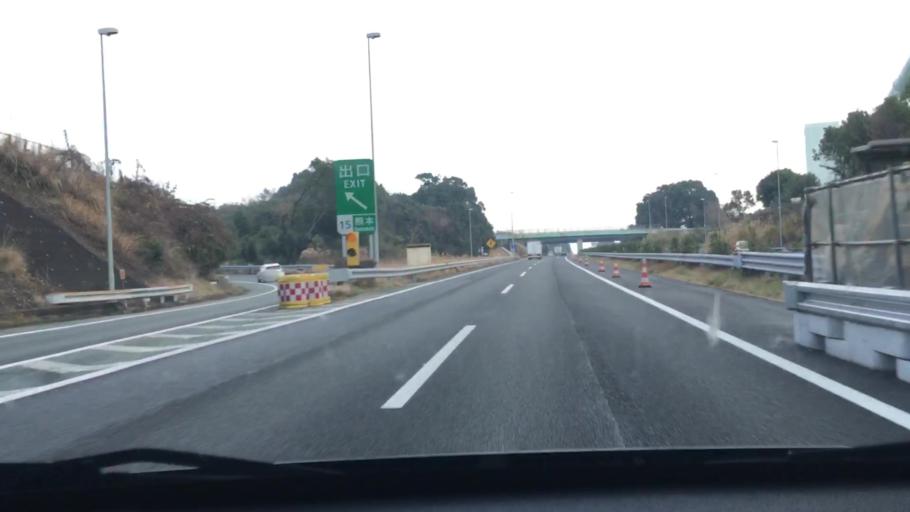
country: JP
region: Kumamoto
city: Kumamoto
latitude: 32.8364
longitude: 130.7782
